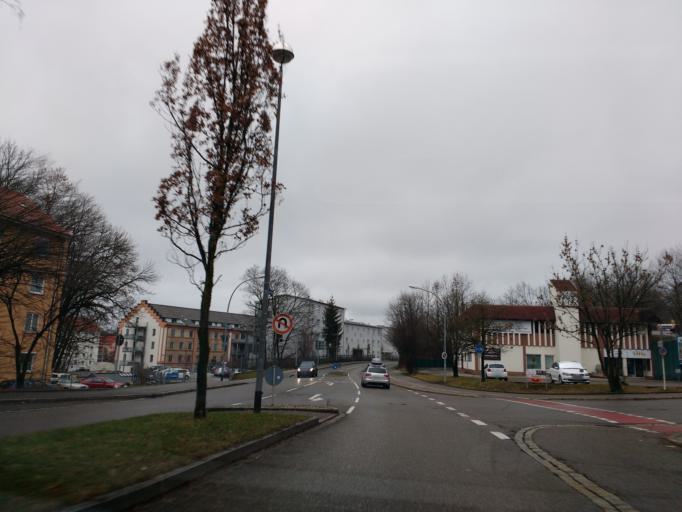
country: DE
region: Bavaria
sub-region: Swabia
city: Kempten (Allgaeu)
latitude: 47.7166
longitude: 10.3251
